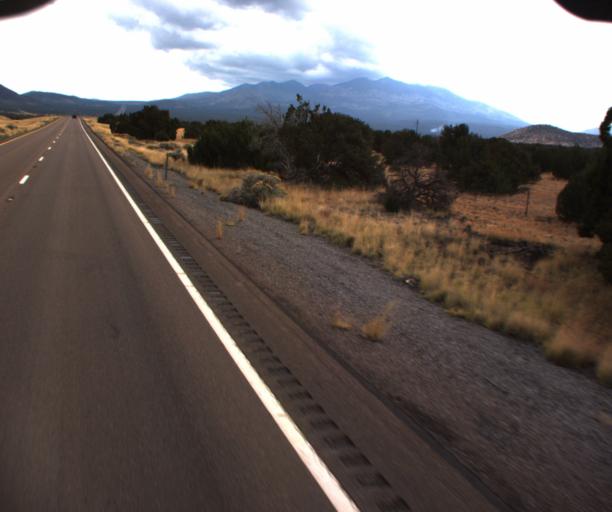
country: US
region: Arizona
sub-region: Coconino County
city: Flagstaff
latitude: 35.4743
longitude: -111.5578
